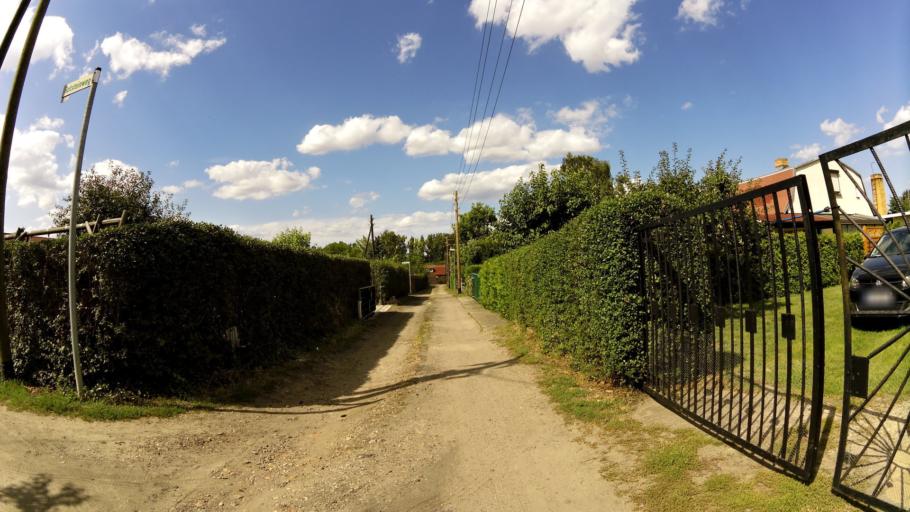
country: DE
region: Berlin
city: Niederschonhausen
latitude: 52.5977
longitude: 13.3939
